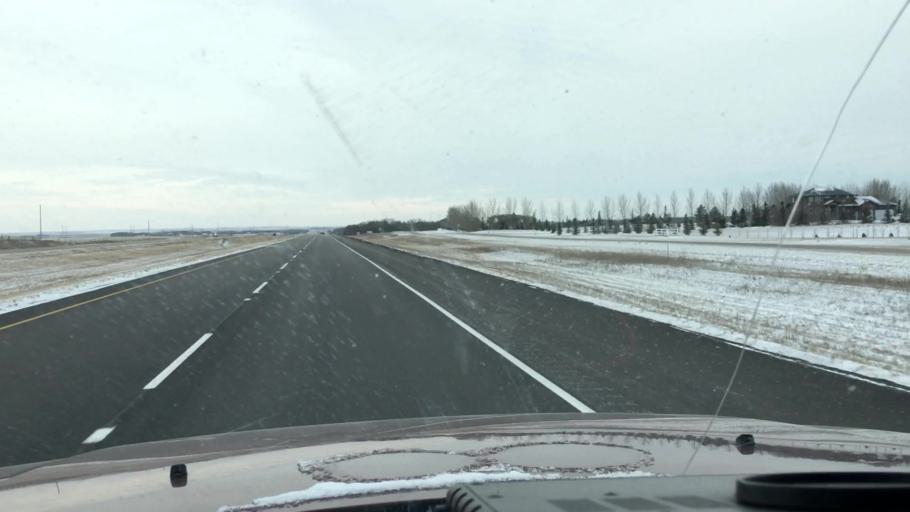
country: CA
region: Saskatchewan
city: Saskatoon
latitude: 51.9080
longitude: -106.5251
